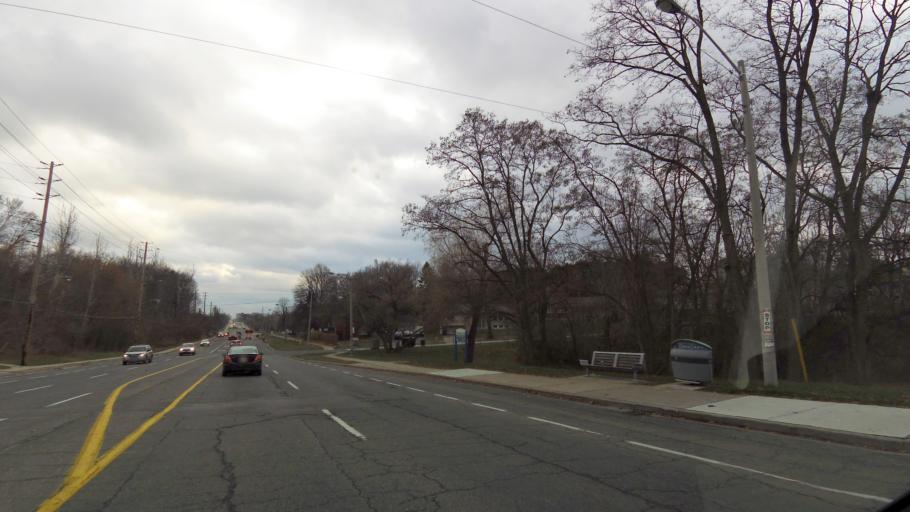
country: CA
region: Ontario
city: Etobicoke
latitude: 43.7347
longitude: -79.5642
